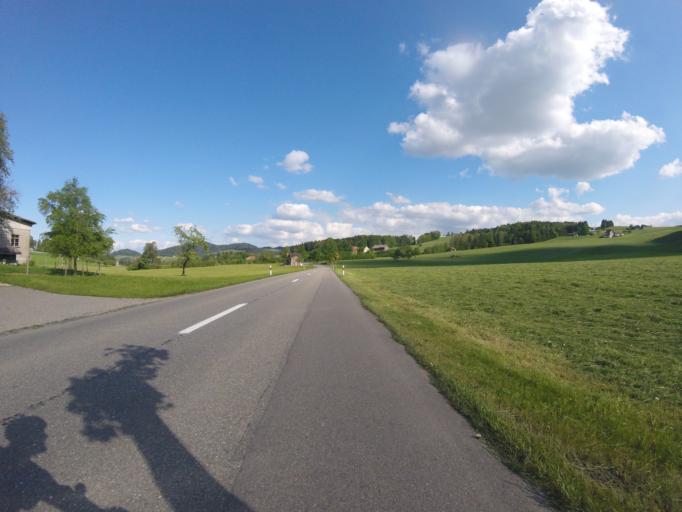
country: CH
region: Saint Gallen
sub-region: Wahlkreis Wil
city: Degersheim
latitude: 47.3876
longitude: 9.1947
